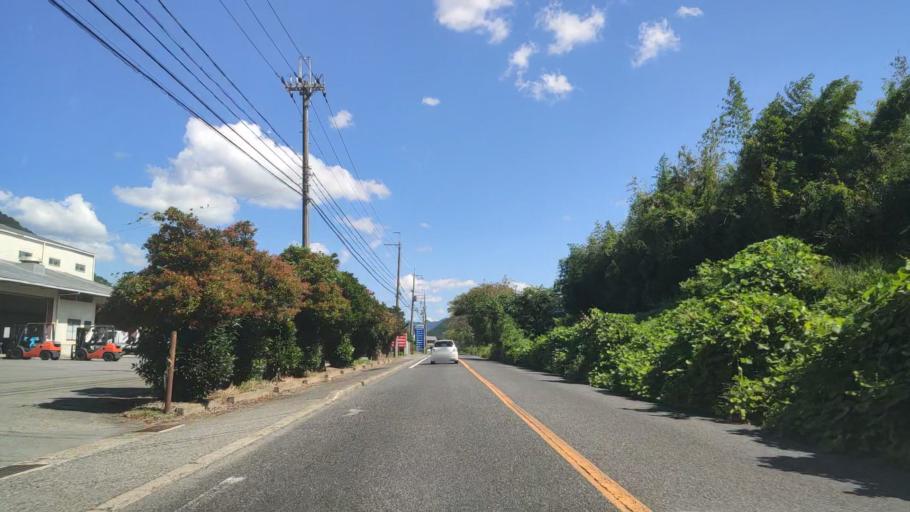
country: JP
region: Hyogo
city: Nishiwaki
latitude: 35.0595
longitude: 135.0003
